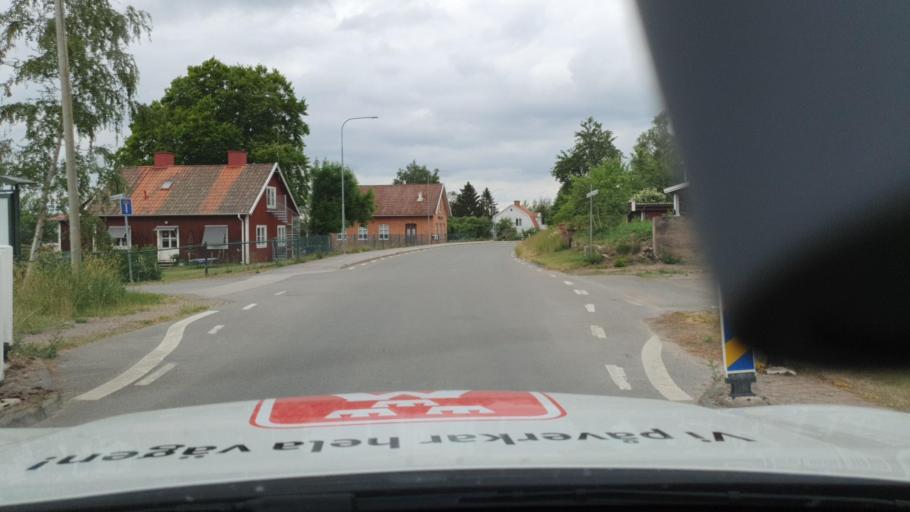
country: SE
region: Vaestra Goetaland
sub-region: Tidaholms Kommun
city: Olofstorp
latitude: 58.3005
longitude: 14.1006
